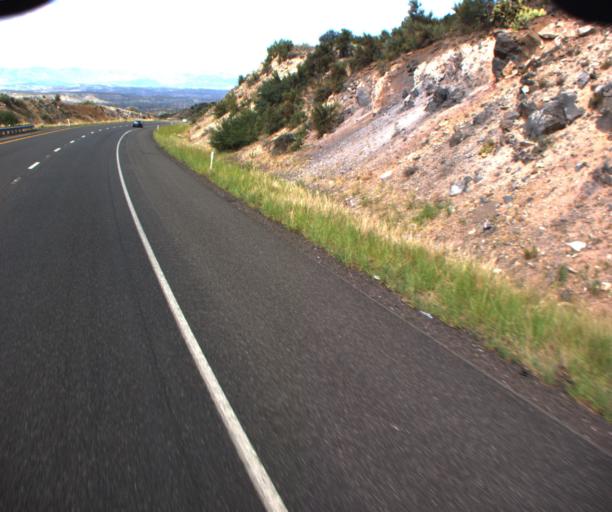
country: US
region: Arizona
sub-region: Yavapai County
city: Big Park
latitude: 34.7119
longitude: -111.7307
